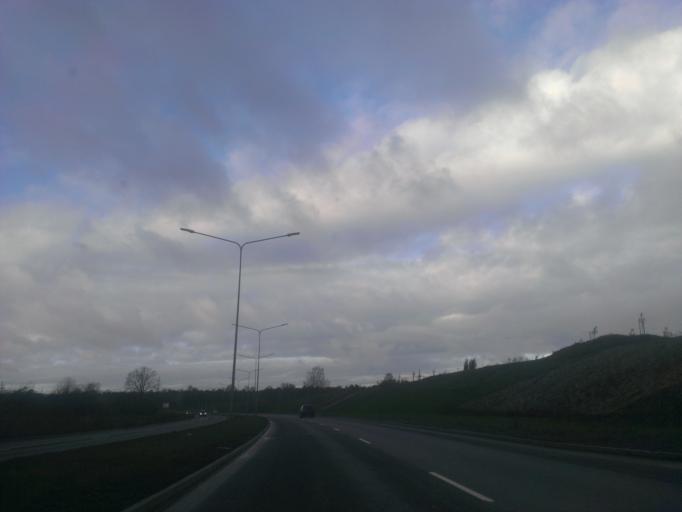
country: LV
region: Riga
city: Jaunciems
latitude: 56.9911
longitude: 24.1571
